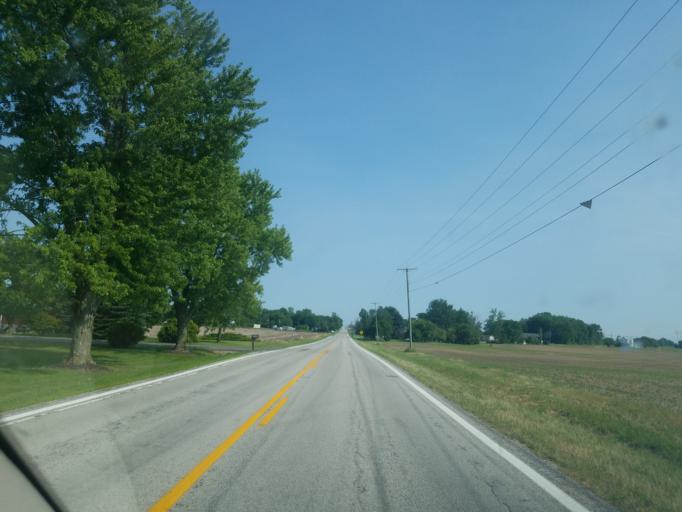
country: US
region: Ohio
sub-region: Wyandot County
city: Carey
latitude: 41.0324
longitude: -83.3014
